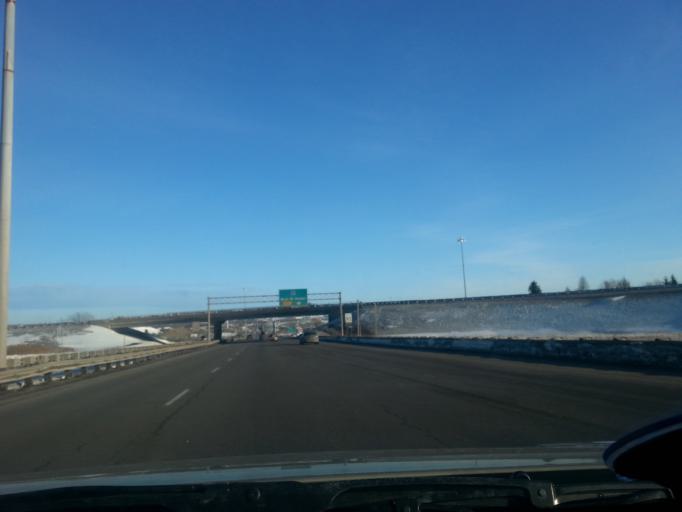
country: CA
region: Quebec
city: L'Ancienne-Lorette
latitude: 46.8108
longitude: -71.3381
